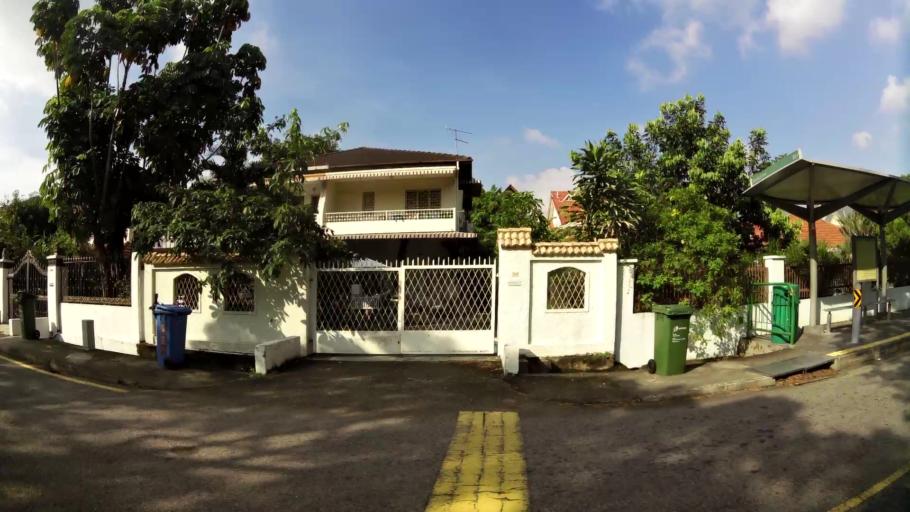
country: SG
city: Singapore
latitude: 1.3147
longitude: 103.9190
